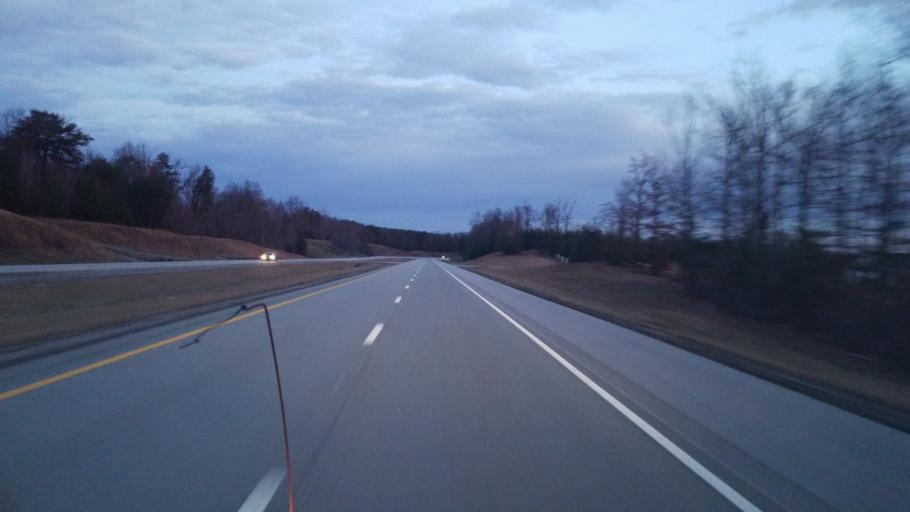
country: US
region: Tennessee
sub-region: Van Buren County
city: Spencer
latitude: 35.6882
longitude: -85.4792
